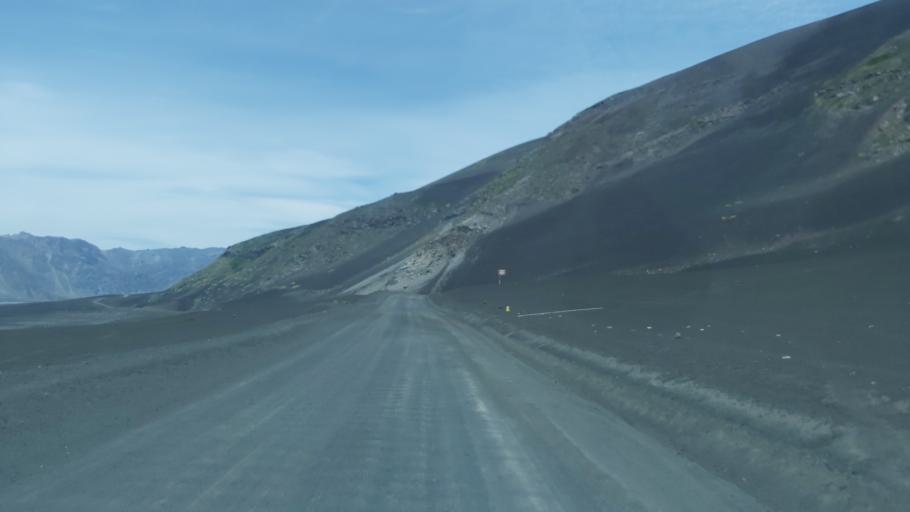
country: AR
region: Neuquen
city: Andacollo
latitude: -37.4009
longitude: -71.3023
